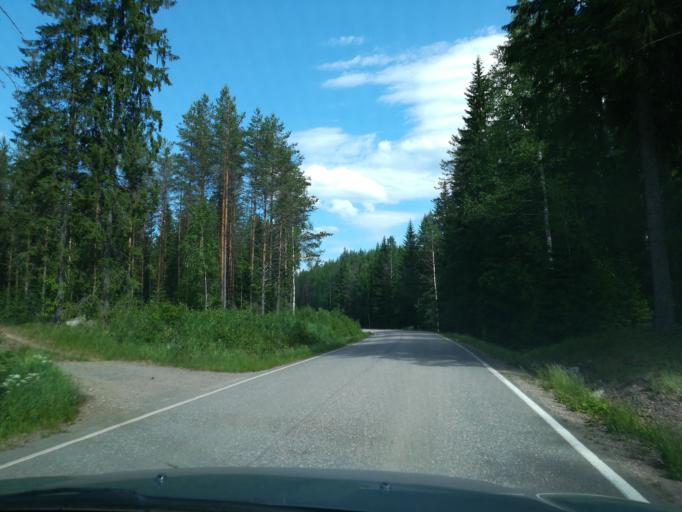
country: FI
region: South Karelia
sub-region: Imatra
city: Ruokolahti
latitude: 61.4742
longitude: 28.7957
